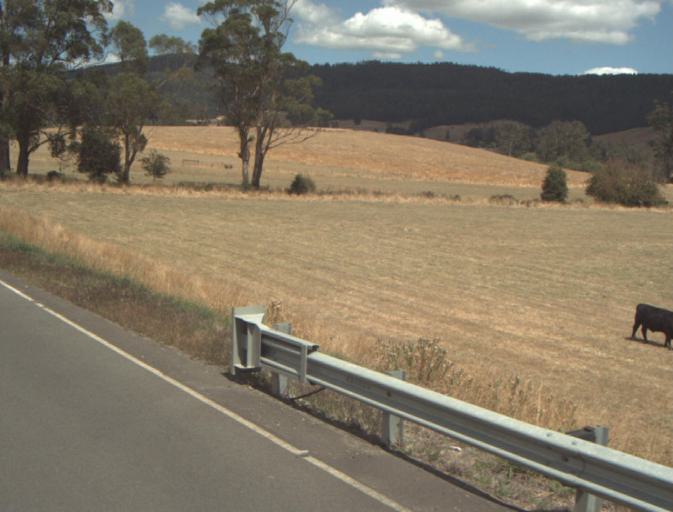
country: AU
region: Tasmania
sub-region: Launceston
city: Mayfield
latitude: -41.2198
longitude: 147.1376
